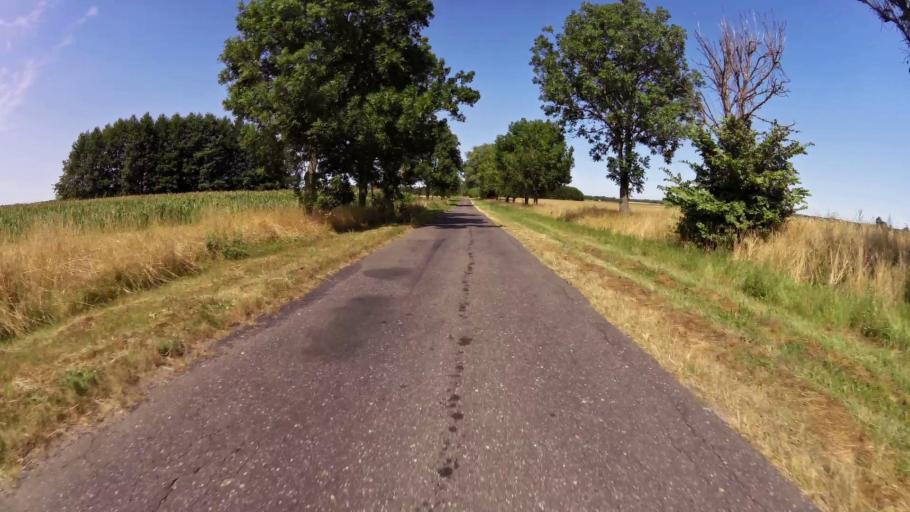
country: PL
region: West Pomeranian Voivodeship
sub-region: Powiat stargardzki
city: Suchan
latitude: 53.2818
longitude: 15.3622
